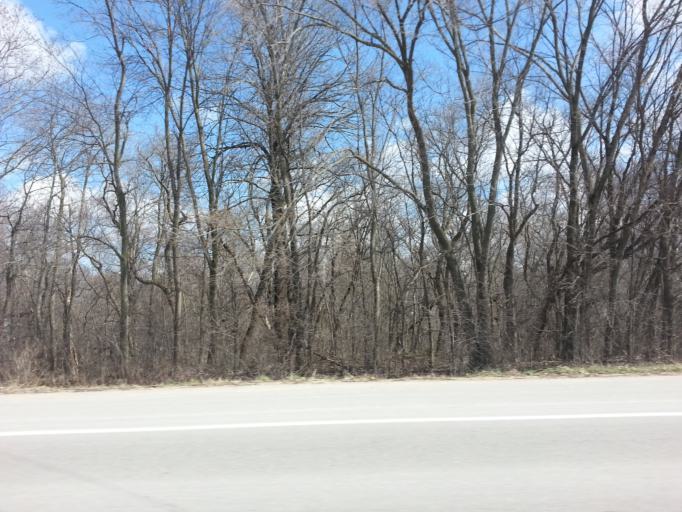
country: US
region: Minnesota
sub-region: Goodhue County
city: Kenyon
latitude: 44.2808
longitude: -92.9797
